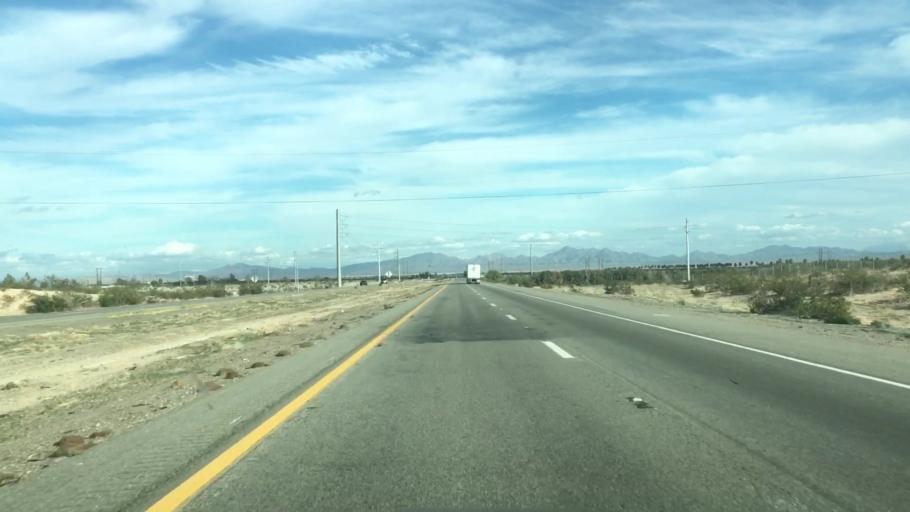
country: US
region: California
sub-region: Riverside County
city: Mesa Verde
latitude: 33.6066
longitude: -114.7014
